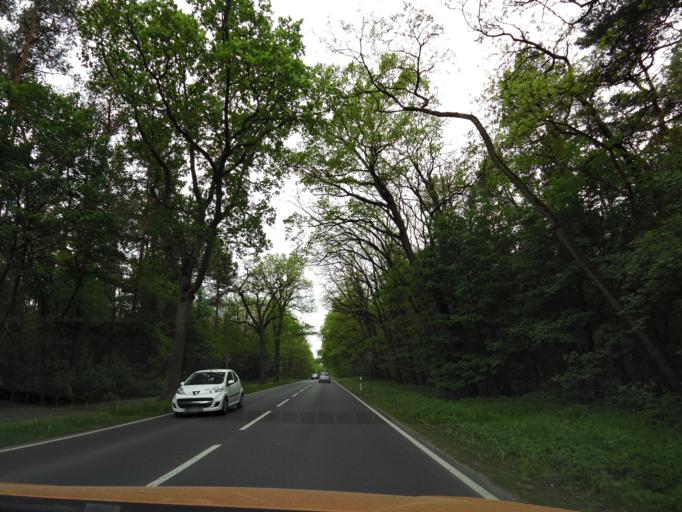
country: DE
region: Brandenburg
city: Beelitz
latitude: 52.2586
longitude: 12.9915
